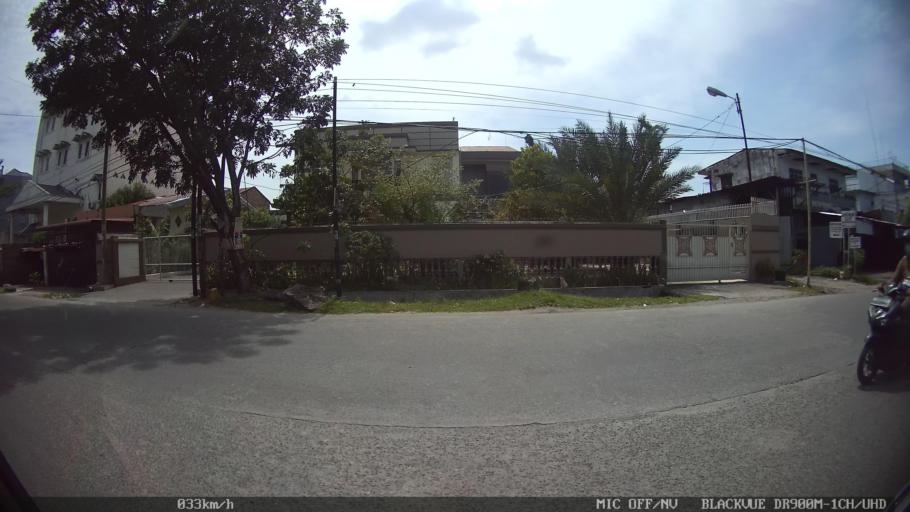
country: ID
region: North Sumatra
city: Medan
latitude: 3.5830
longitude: 98.6413
